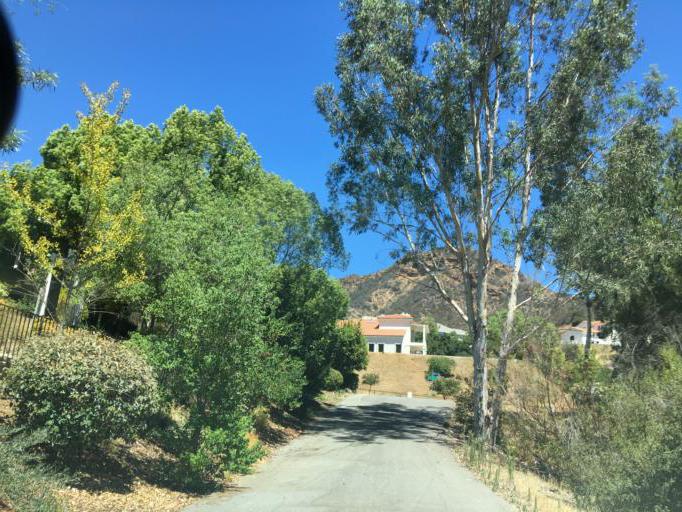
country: US
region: California
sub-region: Los Angeles County
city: Agoura Hills
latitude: 34.1140
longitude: -118.7737
